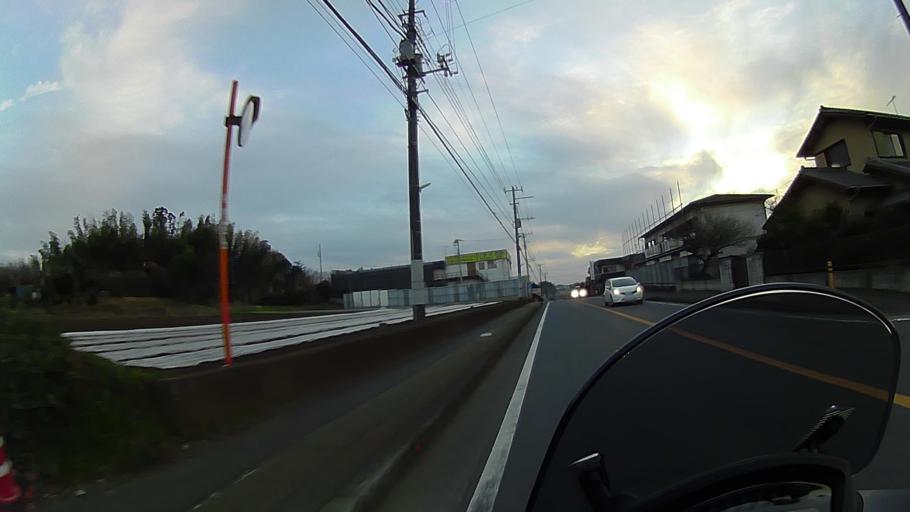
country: JP
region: Kanagawa
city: Atsugi
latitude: 35.4124
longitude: 139.4167
